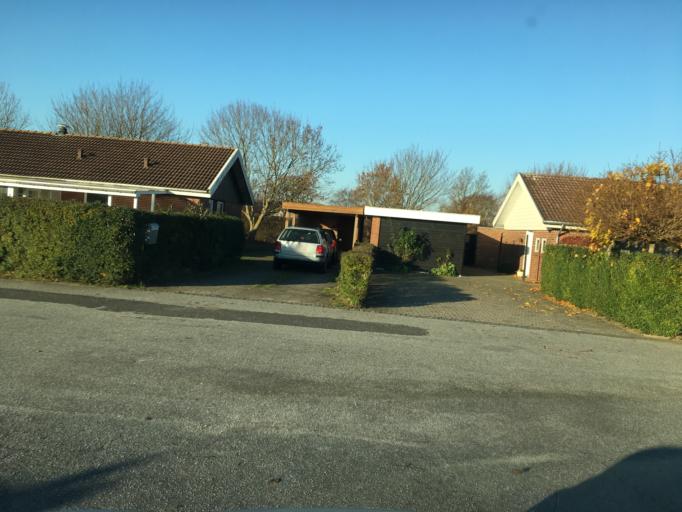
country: DK
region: South Denmark
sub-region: Tonder Kommune
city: Tonder
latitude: 54.9365
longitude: 8.8474
